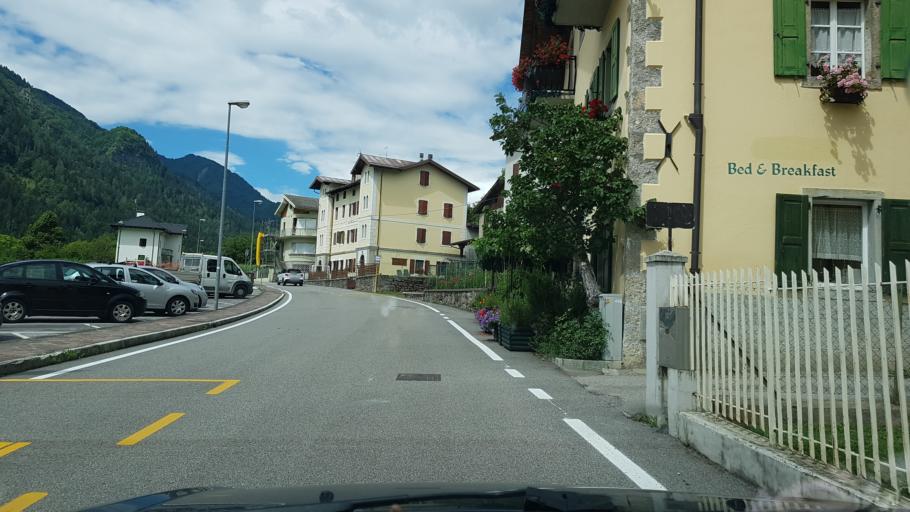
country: IT
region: Friuli Venezia Giulia
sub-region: Provincia di Udine
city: Cercivento
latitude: 46.5274
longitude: 12.9921
